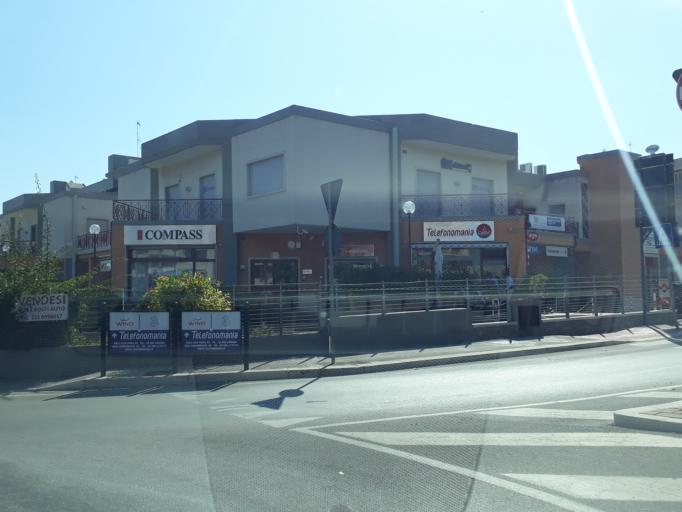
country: IT
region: Apulia
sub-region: Provincia di Bari
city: Monopoli
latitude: 40.9483
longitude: 17.2904
